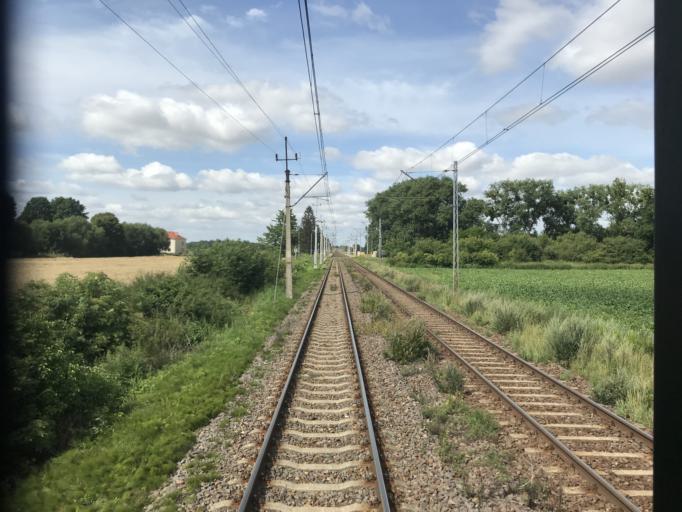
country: PL
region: Pomeranian Voivodeship
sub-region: Powiat malborski
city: Stare Pole
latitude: 54.0379
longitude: 19.1220
